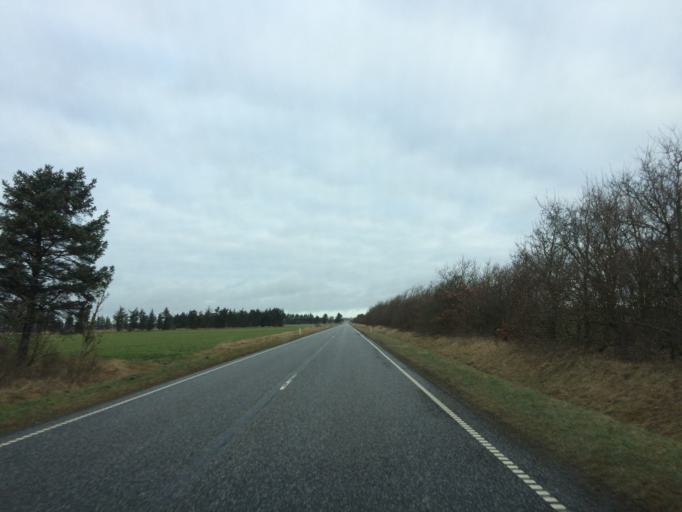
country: DK
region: Central Jutland
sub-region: Holstebro Kommune
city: Holstebro
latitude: 56.3865
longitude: 8.4530
